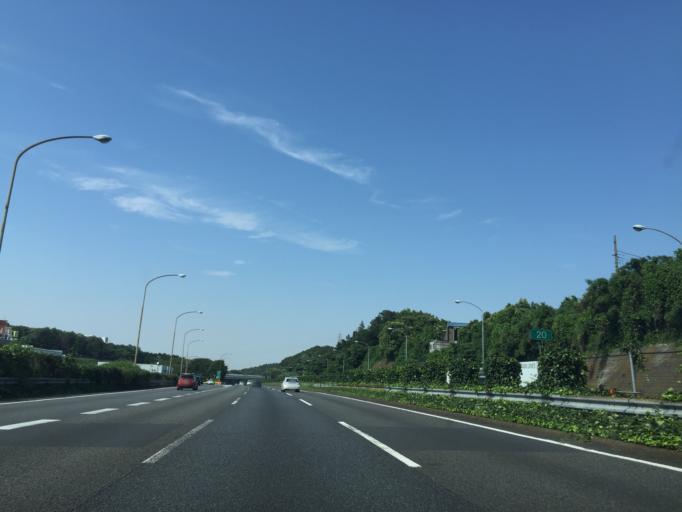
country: JP
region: Kanagawa
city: Minami-rinkan
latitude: 35.5056
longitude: 139.4822
